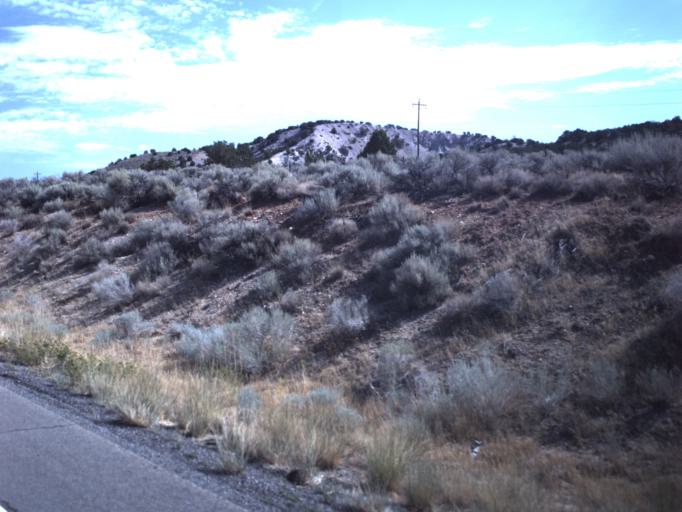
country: US
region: Utah
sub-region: Sanpete County
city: Gunnison
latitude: 39.4141
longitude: -111.9243
